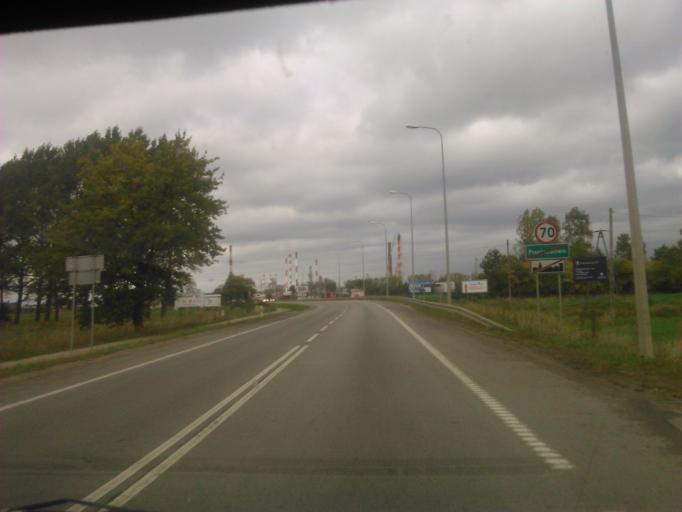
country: PL
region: Pomeranian Voivodeship
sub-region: Gdansk
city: Gdansk
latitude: 54.3325
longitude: 18.7439
